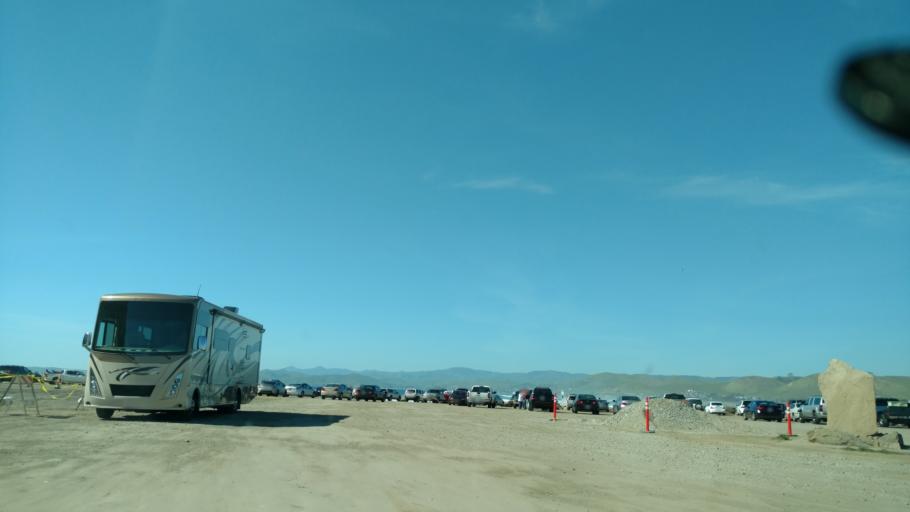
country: US
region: California
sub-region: San Luis Obispo County
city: Morro Bay
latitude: 35.3704
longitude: -120.8652
